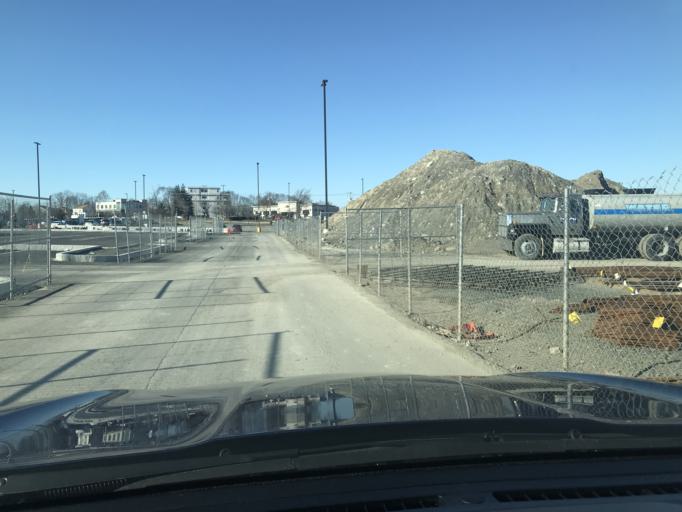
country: US
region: Massachusetts
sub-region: Essex County
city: Peabody
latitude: 42.5421
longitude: -70.9433
